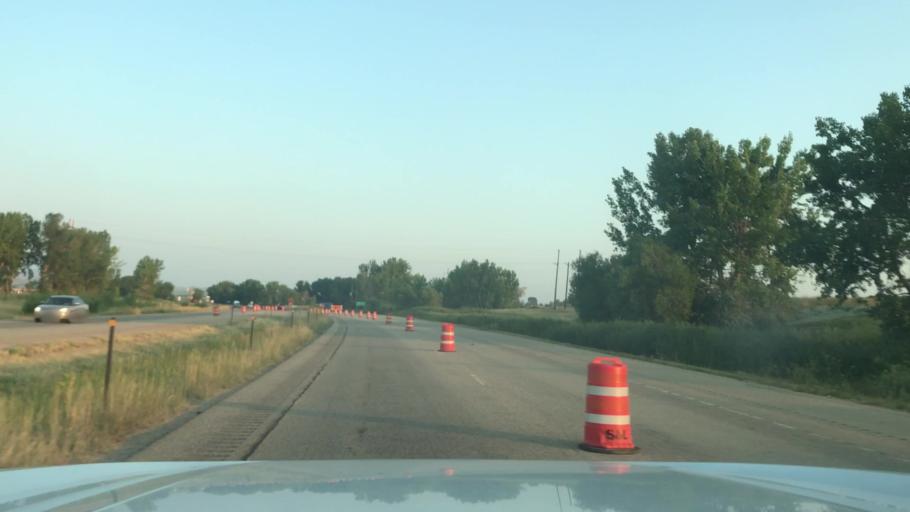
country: US
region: Wyoming
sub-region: Sheridan County
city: Sheridan
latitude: 44.8489
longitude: -106.9874
